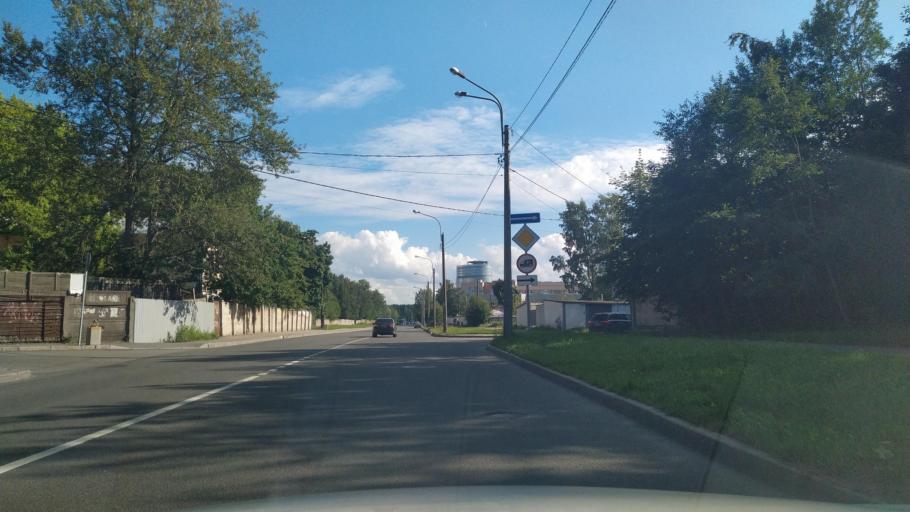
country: RU
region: St.-Petersburg
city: Kolomyagi
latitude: 60.0239
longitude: 30.3017
